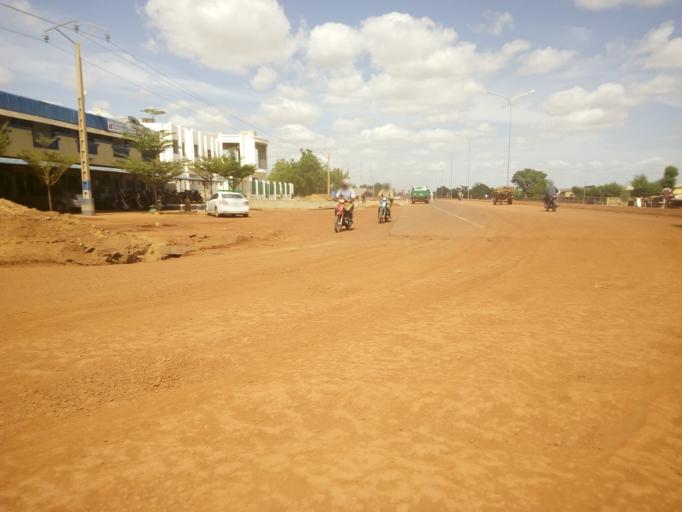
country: ML
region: Segou
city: Segou
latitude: 13.4356
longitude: -6.2342
